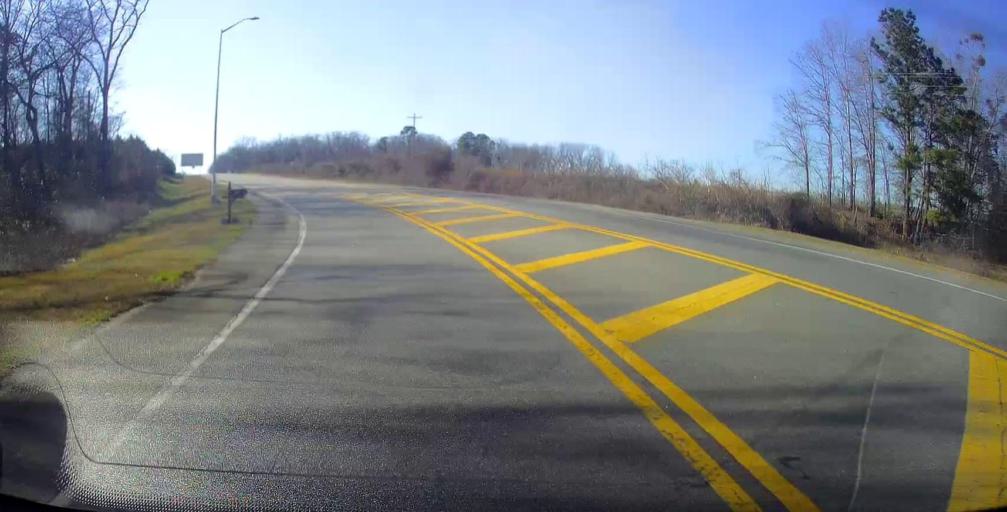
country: US
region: Georgia
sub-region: Sumter County
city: Americus
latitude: 32.1183
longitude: -84.1655
